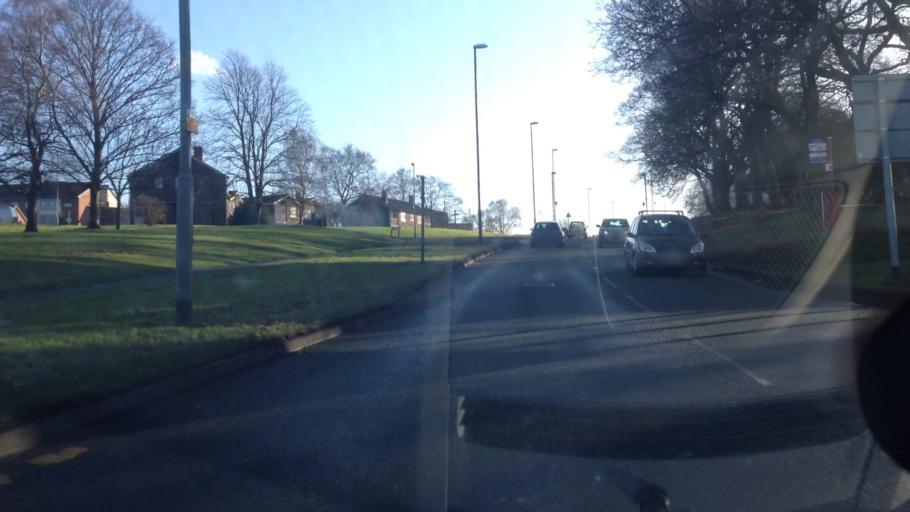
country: GB
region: England
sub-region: City and Borough of Leeds
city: Chapel Allerton
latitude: 53.8449
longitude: -1.5475
